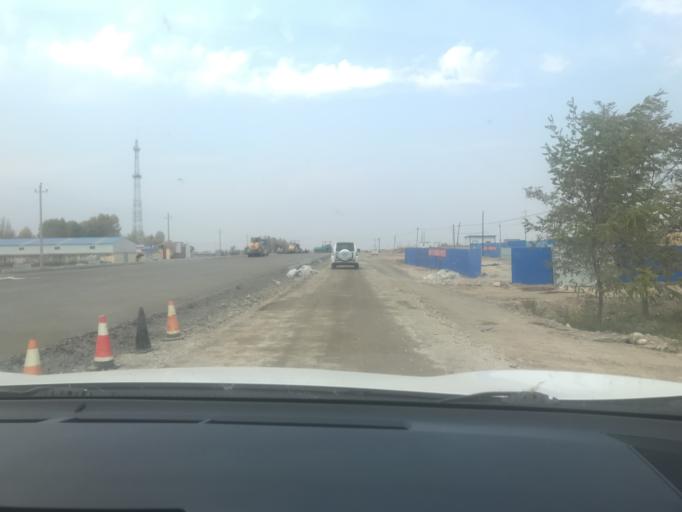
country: CN
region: Gansu Sheng
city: Gulang
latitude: 37.5150
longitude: 102.9008
